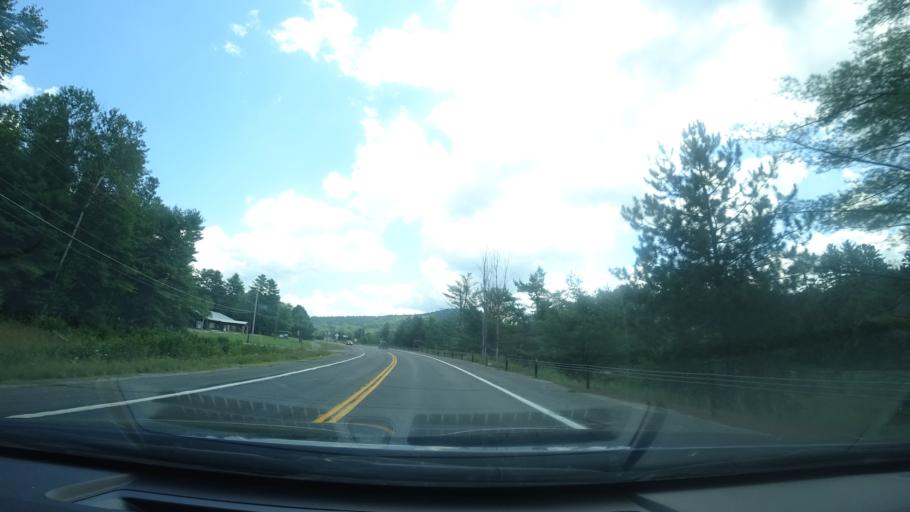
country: US
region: New York
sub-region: Warren County
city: Warrensburg
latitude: 43.6563
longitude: -73.8132
